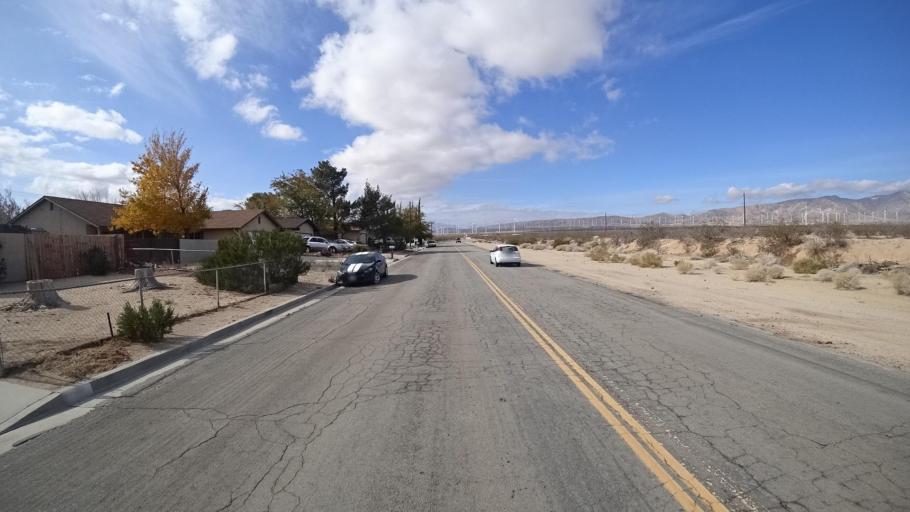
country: US
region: California
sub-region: Kern County
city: Mojave
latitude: 35.0685
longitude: -118.1820
